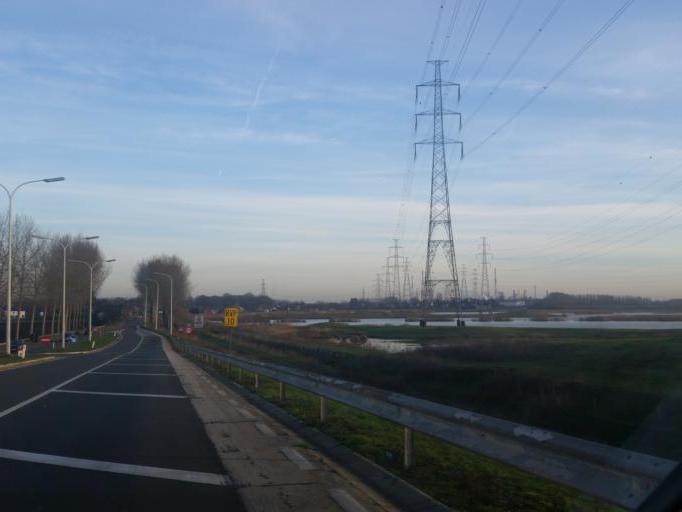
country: BE
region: Flanders
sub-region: Provincie Oost-Vlaanderen
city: Beveren
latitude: 51.2440
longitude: 4.2725
